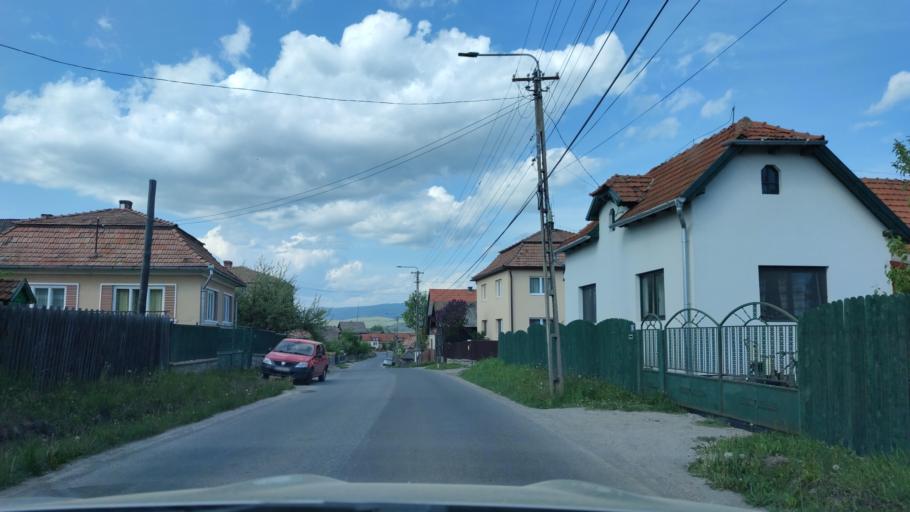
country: RO
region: Harghita
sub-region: Comuna Remetea
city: Remetea
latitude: 46.8034
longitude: 25.4594
